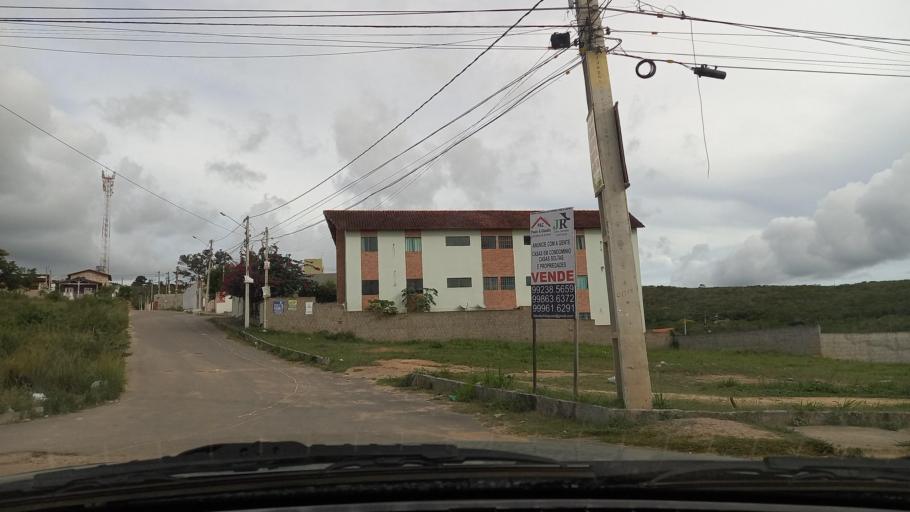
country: BR
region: Pernambuco
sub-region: Gravata
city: Gravata
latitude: -8.2025
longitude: -35.5484
